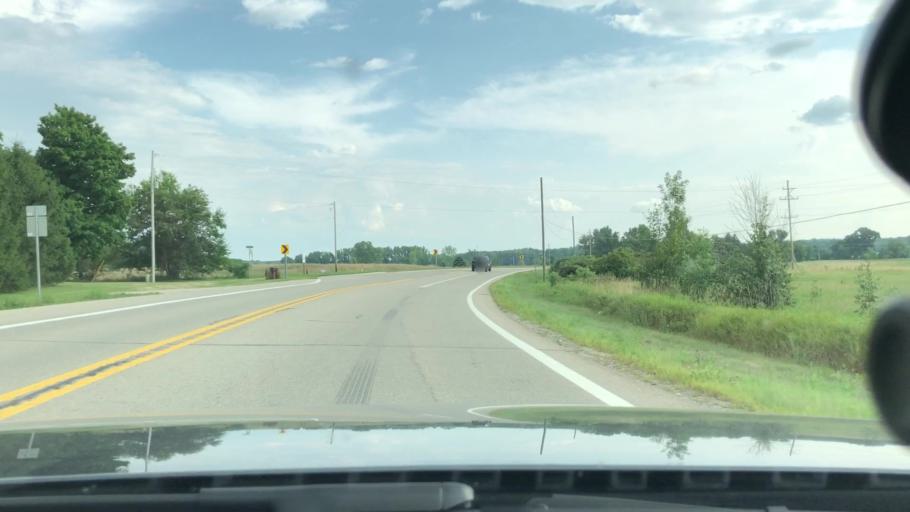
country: US
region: Michigan
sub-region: Washtenaw County
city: Chelsea
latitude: 42.2486
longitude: -84.0334
